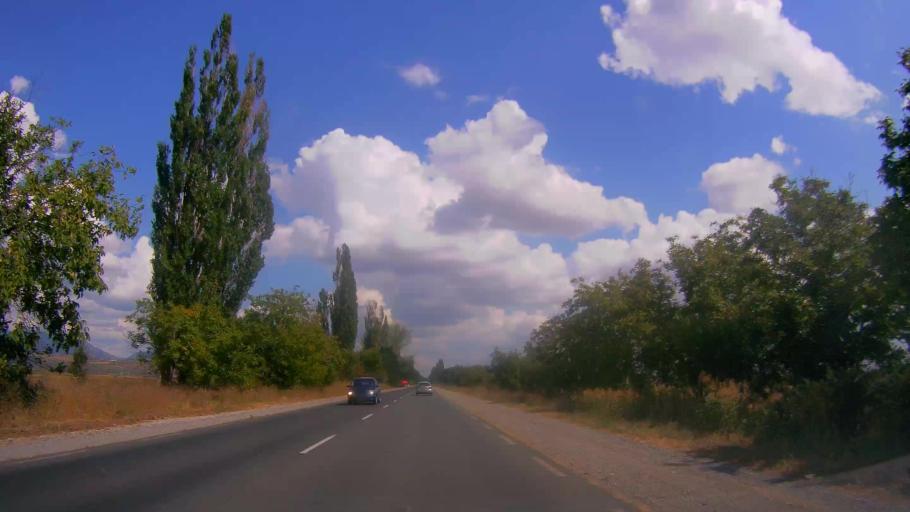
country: BG
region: Sliven
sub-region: Obshtina Sliven
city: Sliven
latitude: 42.6372
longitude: 26.2512
